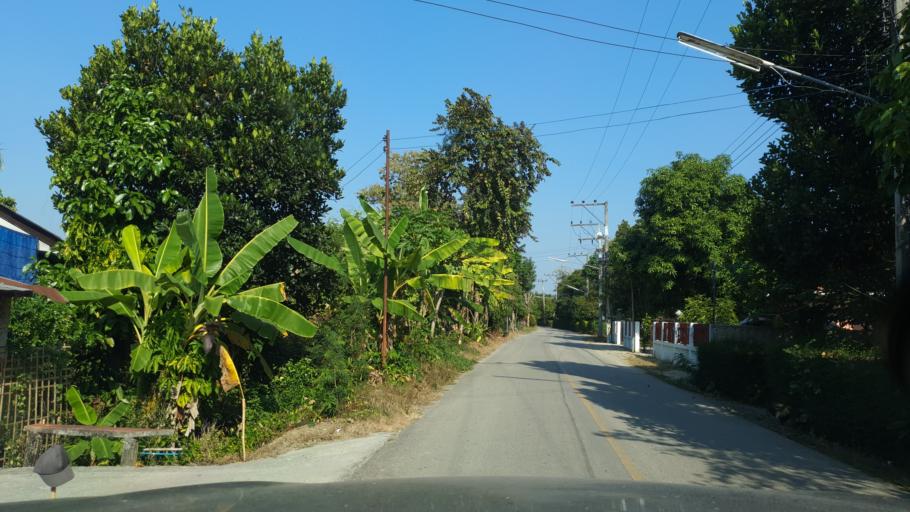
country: TH
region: Chiang Mai
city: Saraphi
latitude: 18.7096
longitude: 99.0744
